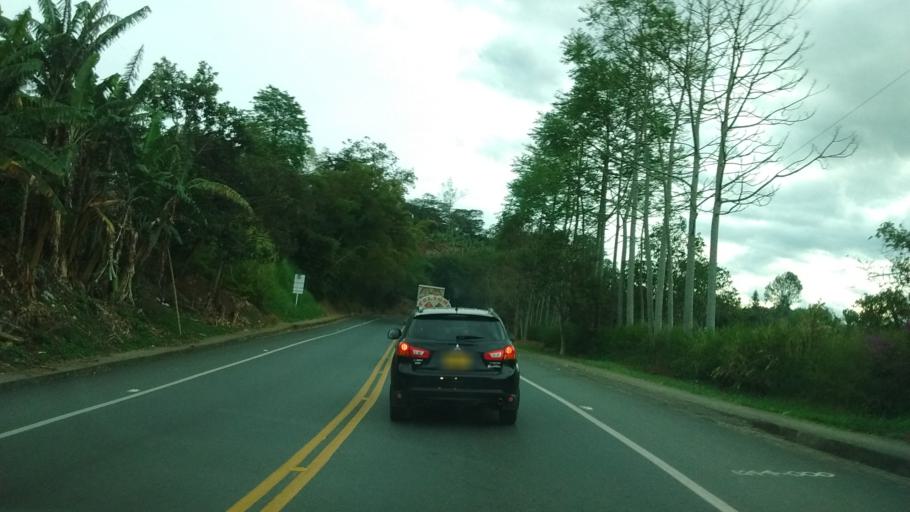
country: CO
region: Cauca
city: Caldono
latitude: 2.7996
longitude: -76.5511
